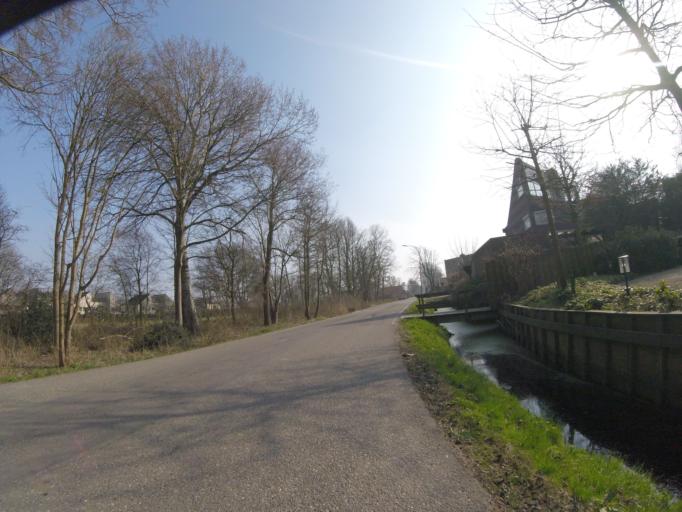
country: NL
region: North Holland
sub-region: Gemeente Heemstede
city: Heemstede
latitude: 52.3514
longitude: 4.6415
